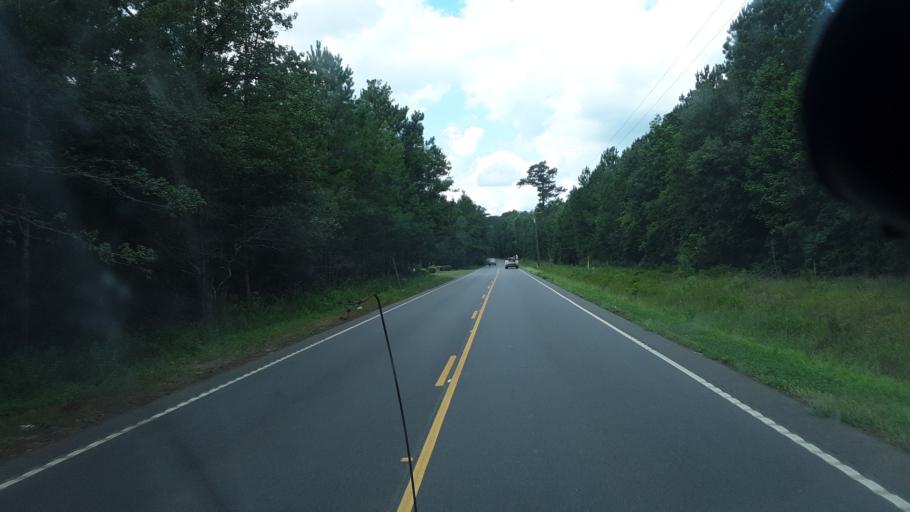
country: US
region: South Carolina
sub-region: Williamsburg County
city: Andrews
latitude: 33.3610
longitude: -79.4703
